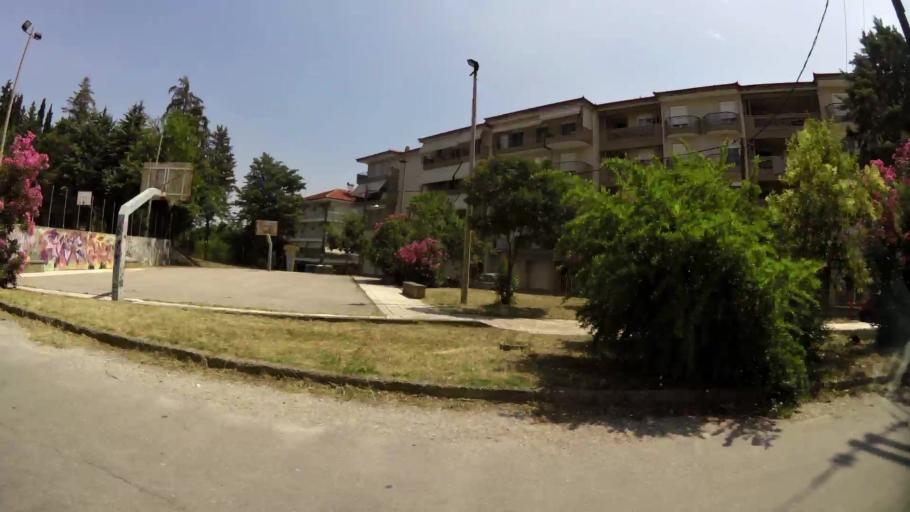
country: GR
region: Central Macedonia
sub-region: Nomos Imathias
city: Veroia
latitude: 40.5115
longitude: 22.2015
